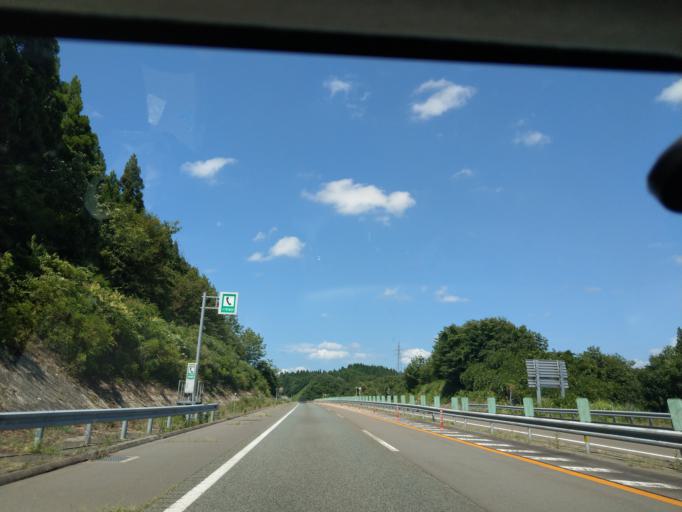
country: JP
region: Akita
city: Akita
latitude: 39.6668
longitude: 140.1884
